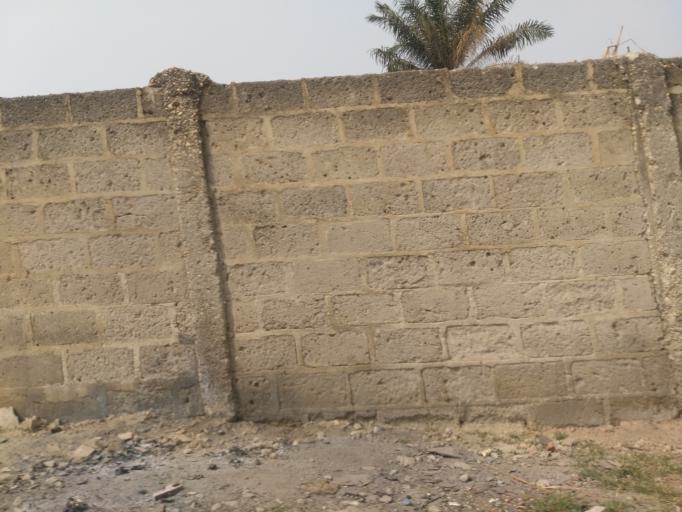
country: GH
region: Ashanti
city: Kumasi
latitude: 6.6933
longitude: -1.6013
